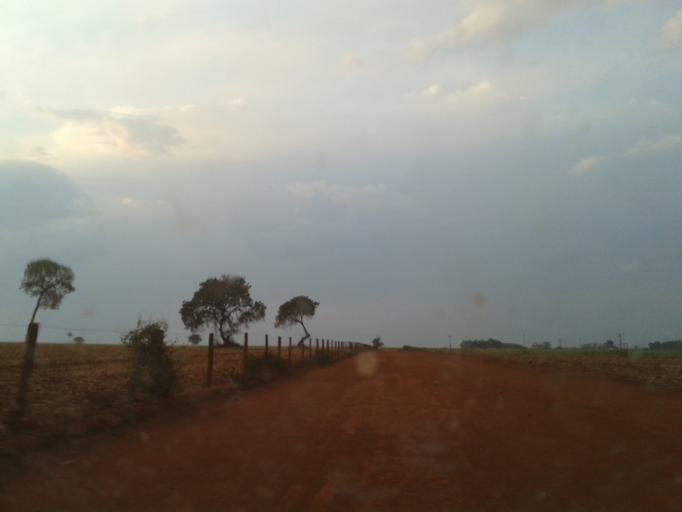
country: BR
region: Minas Gerais
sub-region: Capinopolis
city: Capinopolis
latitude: -18.7190
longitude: -49.6850
